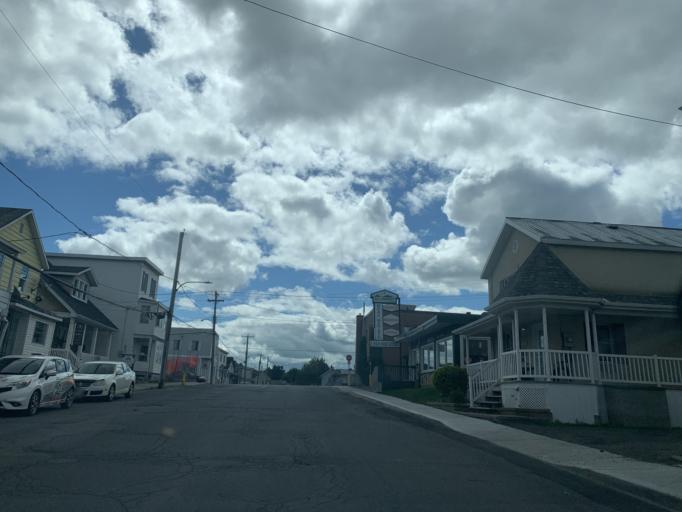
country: CA
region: Ontario
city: Hawkesbury
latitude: 45.6089
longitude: -74.6096
